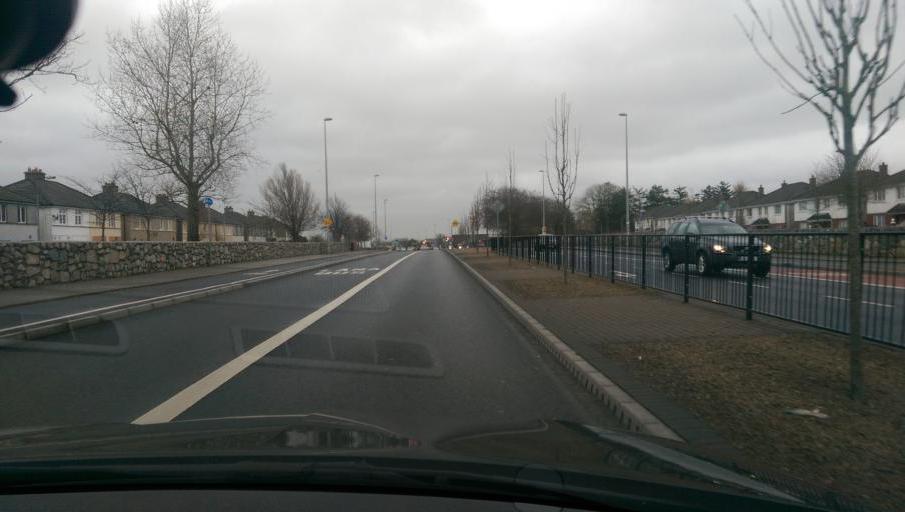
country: IE
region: Connaught
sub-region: County Galway
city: Gaillimh
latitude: 53.2736
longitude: -9.0835
